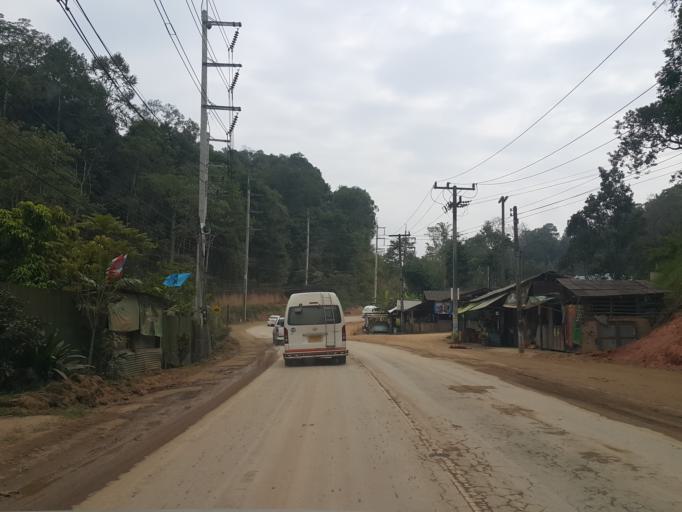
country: TH
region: Chiang Mai
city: Mae Taeng
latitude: 19.1364
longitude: 98.7005
